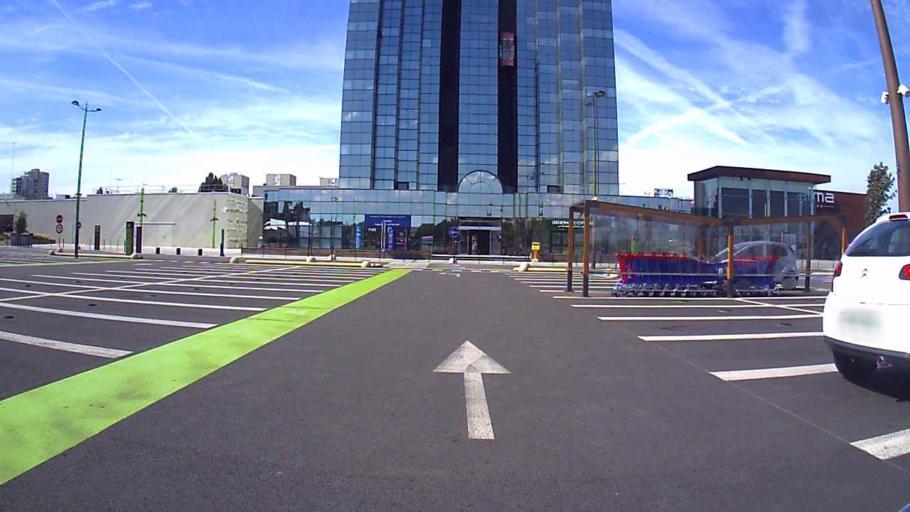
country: FR
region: Brittany
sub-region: Departement d'Ille-et-Vilaine
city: Rennes
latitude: 48.0820
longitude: -1.6790
